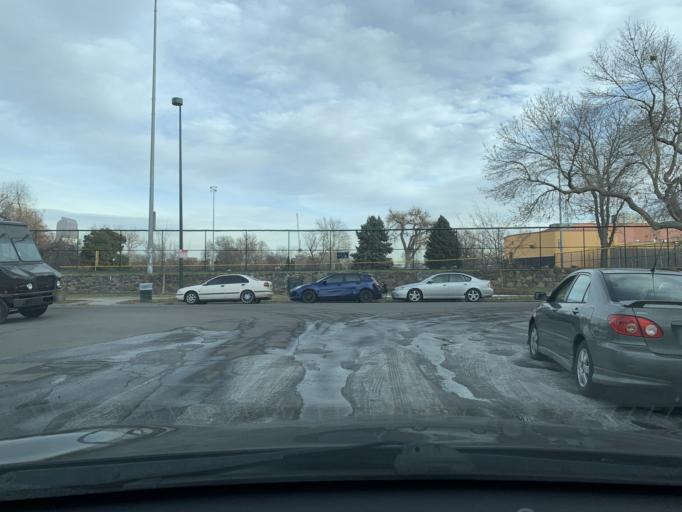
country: US
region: Colorado
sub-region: Denver County
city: Denver
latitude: 39.7353
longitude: -105.0057
